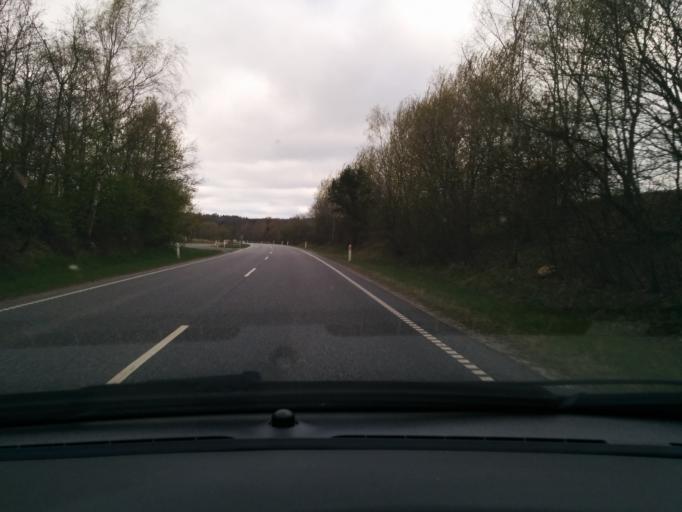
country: DK
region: Central Jutland
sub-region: Favrskov Kommune
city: Hammel
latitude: 56.2565
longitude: 9.8798
